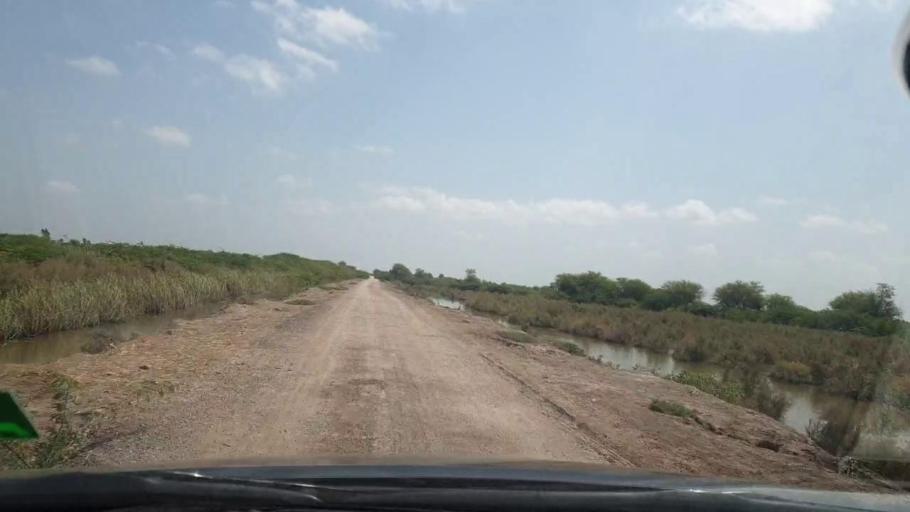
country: PK
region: Sindh
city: Tando Bago
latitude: 24.8607
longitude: 69.1019
